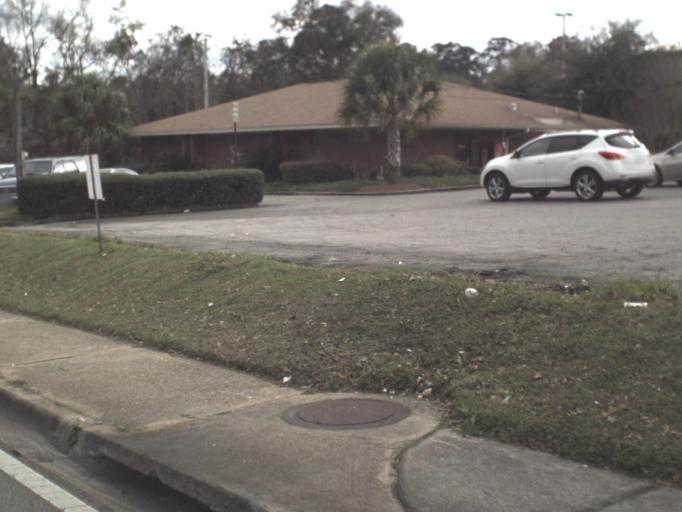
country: US
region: Florida
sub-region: Leon County
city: Tallahassee
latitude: 30.4630
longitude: -84.2822
